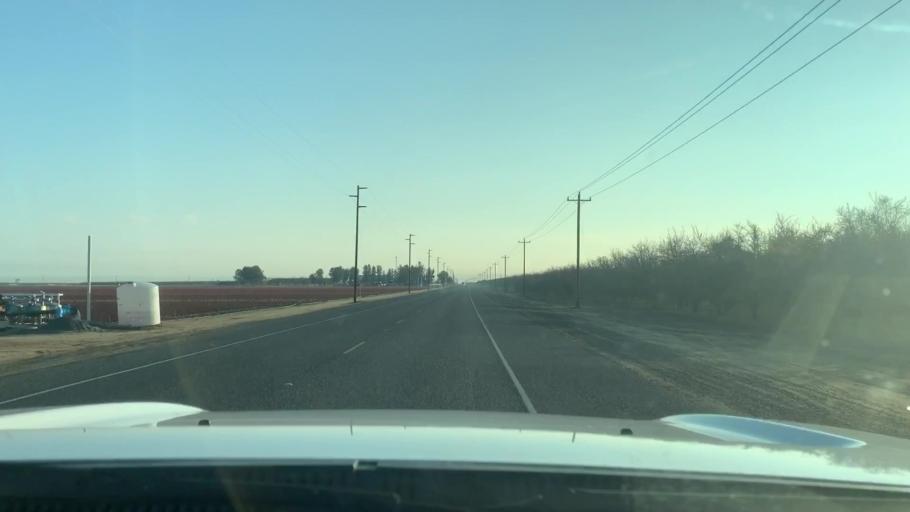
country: US
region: California
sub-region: Kern County
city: Lost Hills
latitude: 35.6011
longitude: -119.5182
